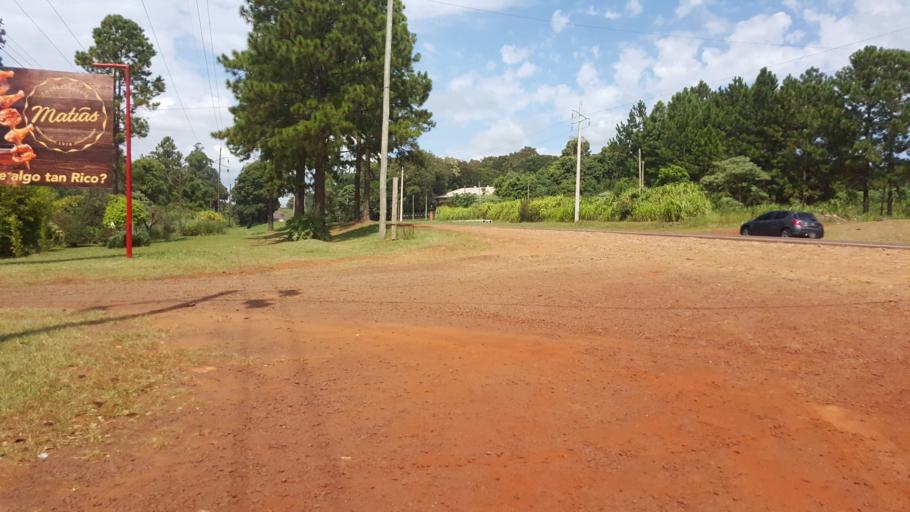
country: AR
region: Misiones
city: Puerto Rico
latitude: -26.8384
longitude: -55.0385
